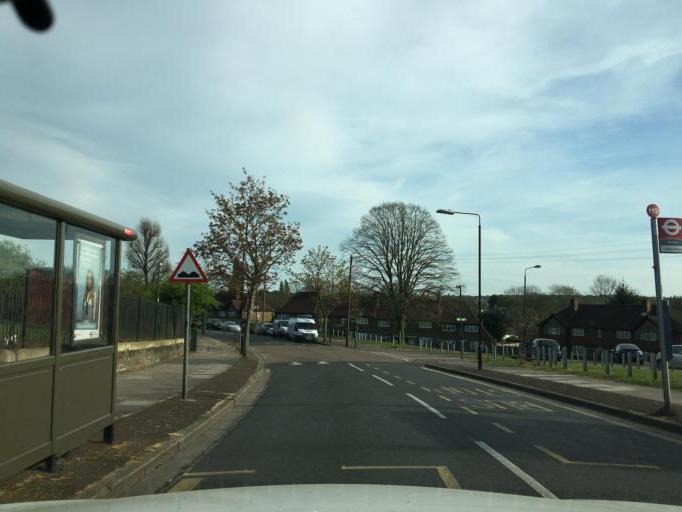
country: GB
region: England
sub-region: Greater London
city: Chislehurst
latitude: 51.4429
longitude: 0.0420
